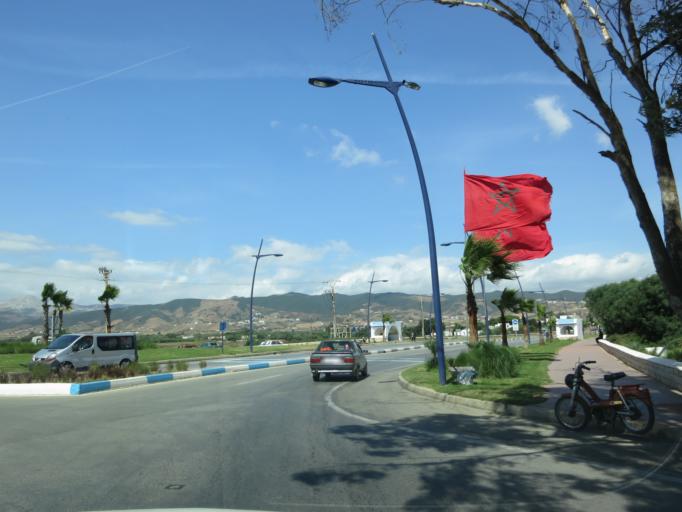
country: ES
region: Ceuta
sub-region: Ceuta
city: Ceuta
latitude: 35.7871
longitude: -5.3528
